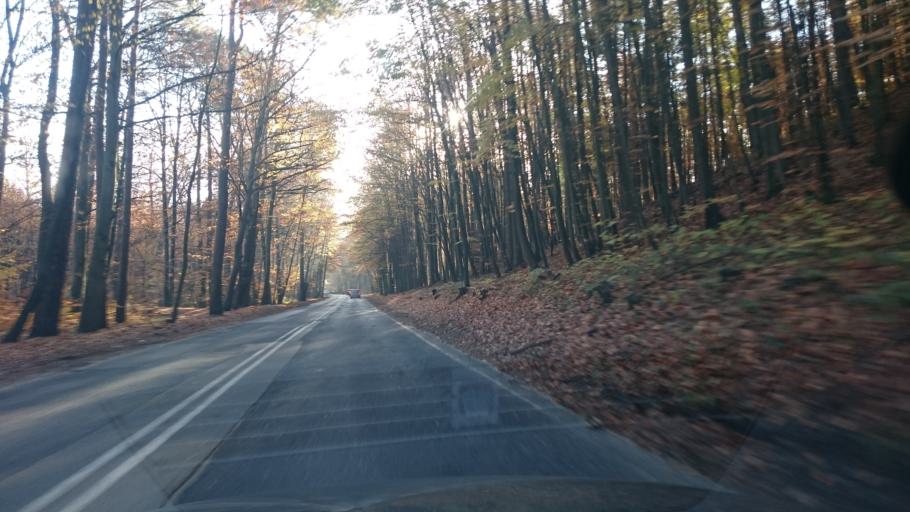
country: PL
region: Pomeranian Voivodeship
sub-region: Gdynia
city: Wielki Kack
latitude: 54.4576
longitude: 18.5130
